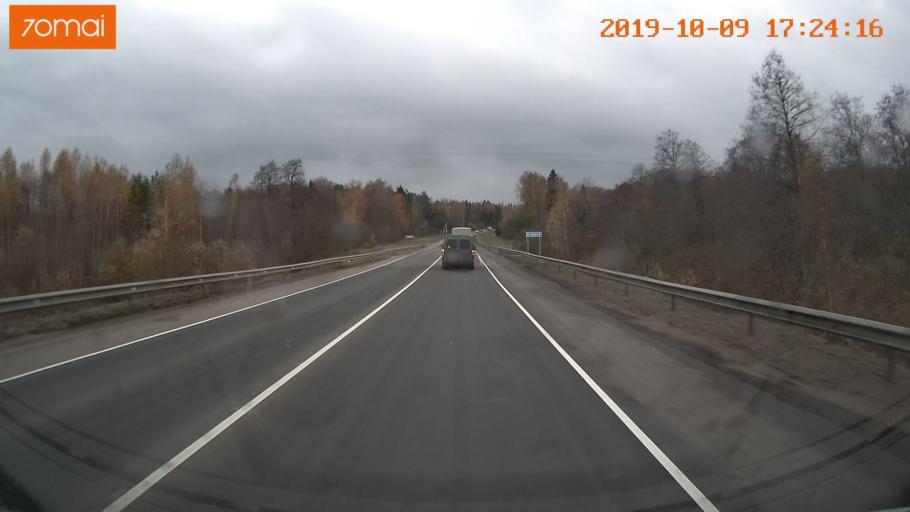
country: RU
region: Ivanovo
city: Furmanov
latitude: 57.1869
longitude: 41.1096
